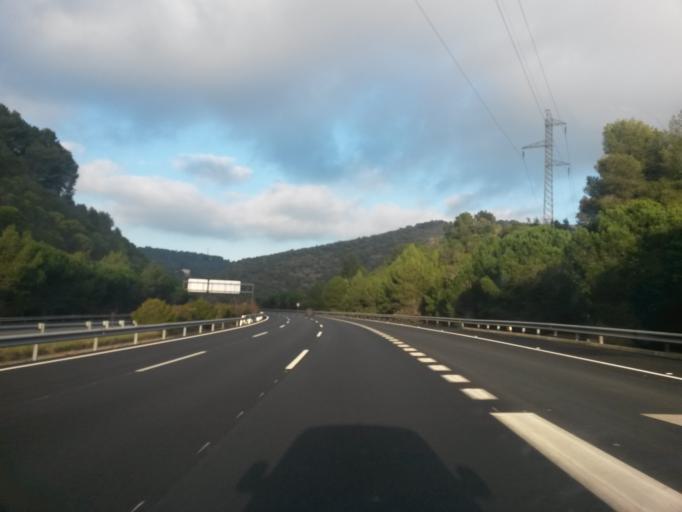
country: ES
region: Catalonia
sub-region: Provincia de Barcelona
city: Pineda de Mar
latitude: 41.6394
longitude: 2.6748
